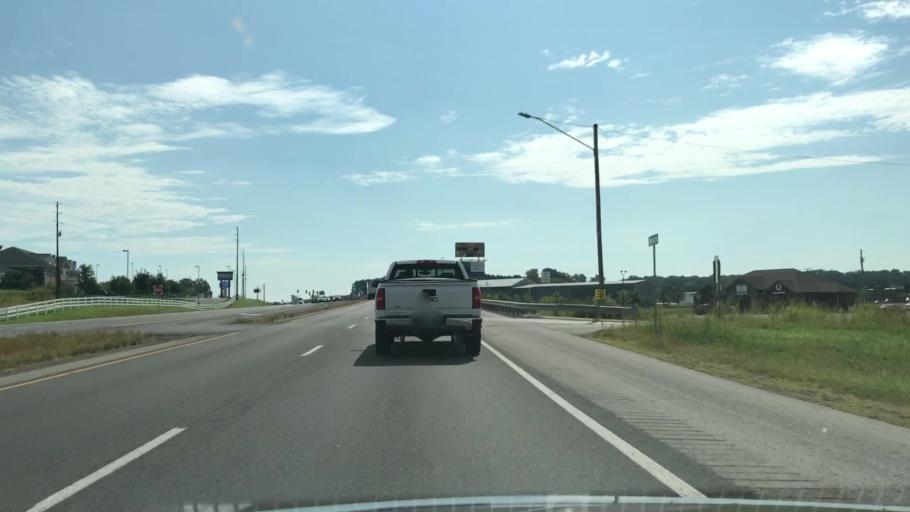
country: US
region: Kentucky
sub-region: Allen County
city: Scottsville
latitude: 36.7569
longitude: -86.2218
